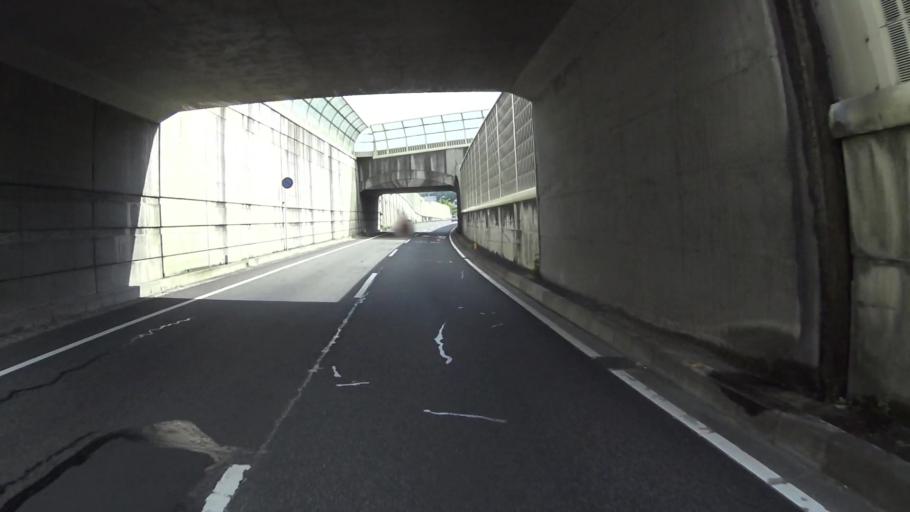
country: JP
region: Shiga Prefecture
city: Otsu-shi
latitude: 35.0434
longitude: 135.8549
